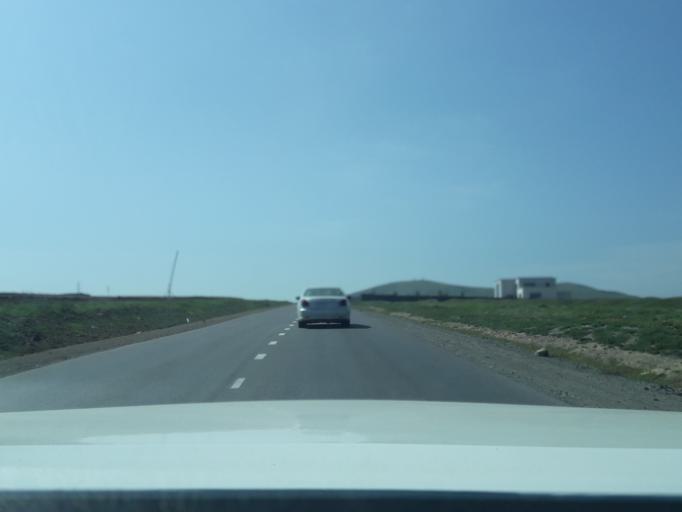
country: MN
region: Ulaanbaatar
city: Ulaanbaatar
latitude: 47.8064
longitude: 106.7499
